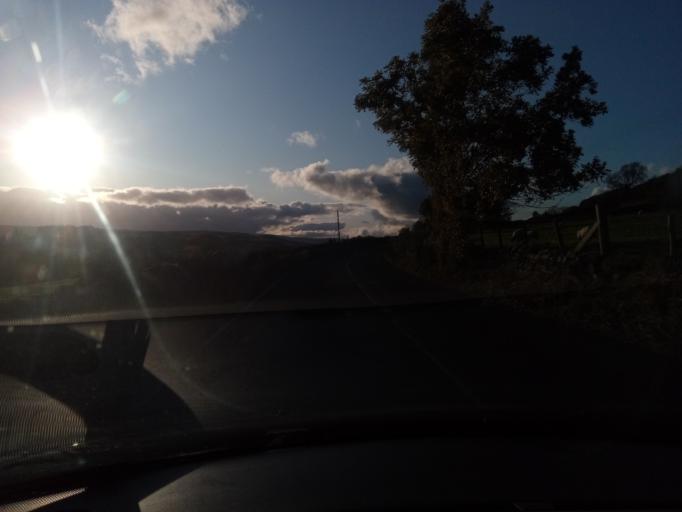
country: GB
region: England
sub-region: County Durham
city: Stanhope
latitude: 54.7458
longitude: -2.0363
